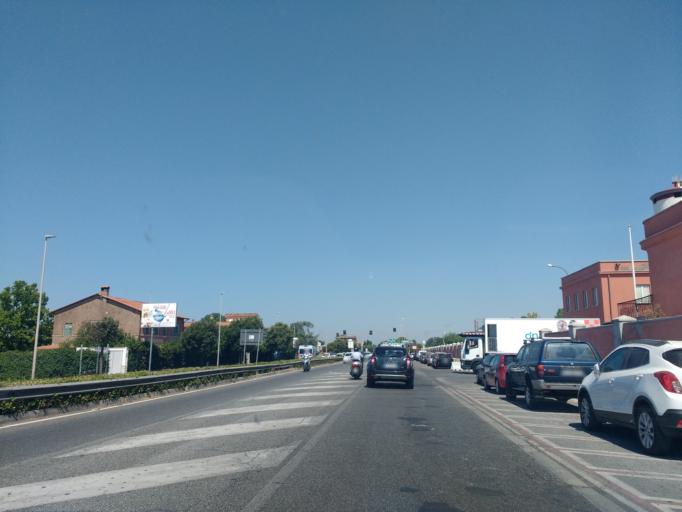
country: IT
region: Latium
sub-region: Citta metropolitana di Roma Capitale
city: Lido di Ostia
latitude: 41.7649
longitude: 12.2645
